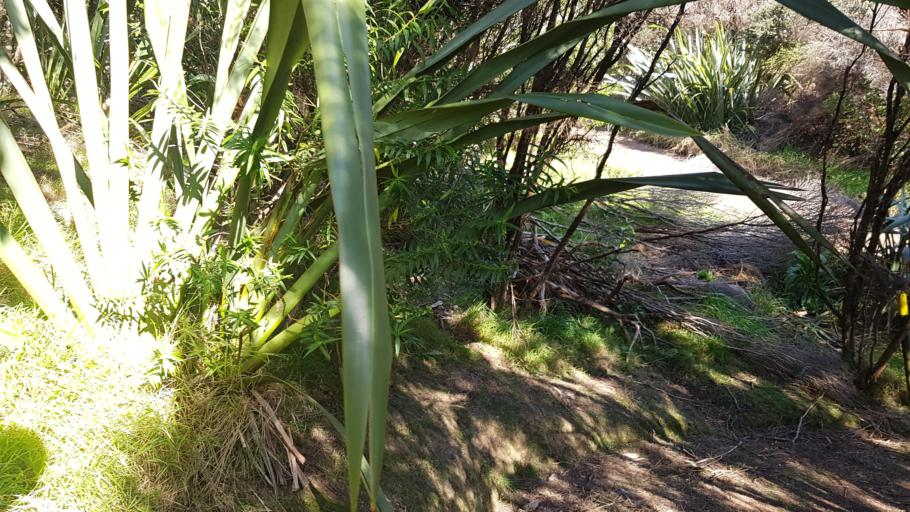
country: NZ
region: Auckland
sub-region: Auckland
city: Pakuranga
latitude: -36.7765
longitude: 174.9940
